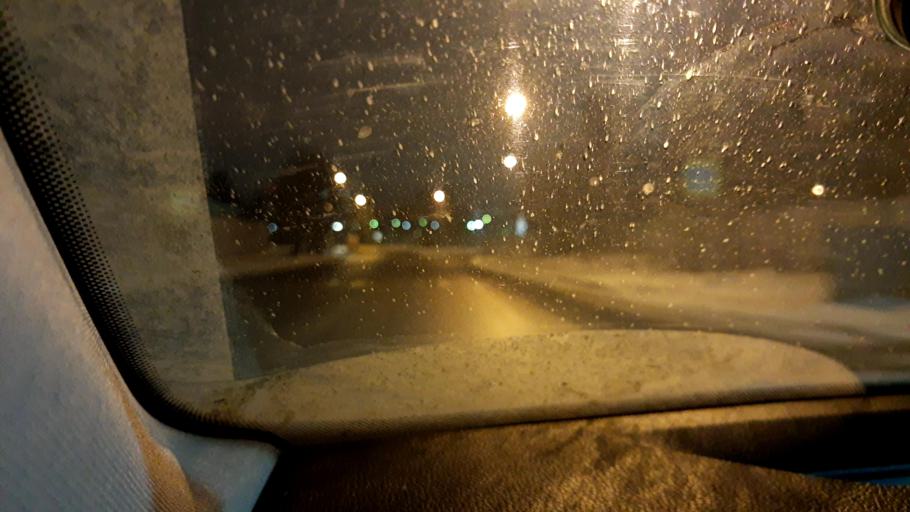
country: RU
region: Moskovskaya
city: Odintsovo
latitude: 55.6722
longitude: 37.2979
